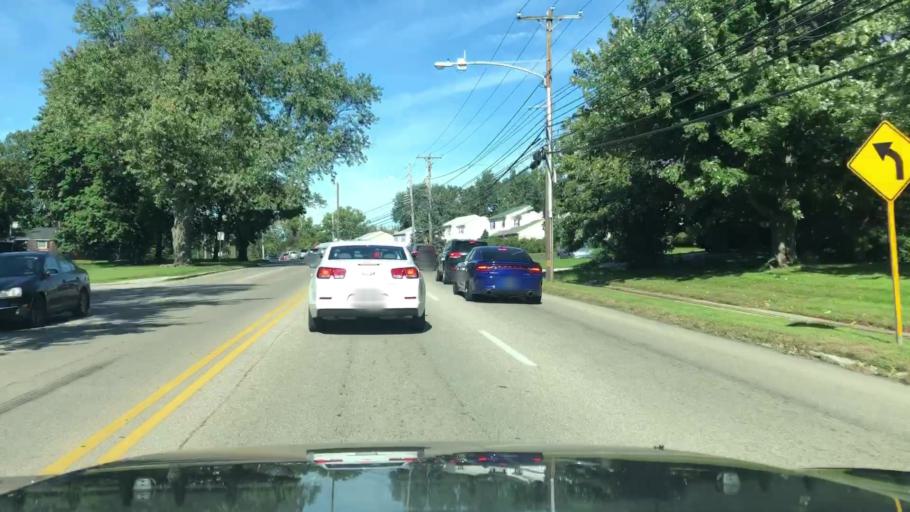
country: US
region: Pennsylvania
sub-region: Montgomery County
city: Norristown
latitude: 40.1350
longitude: -75.3029
